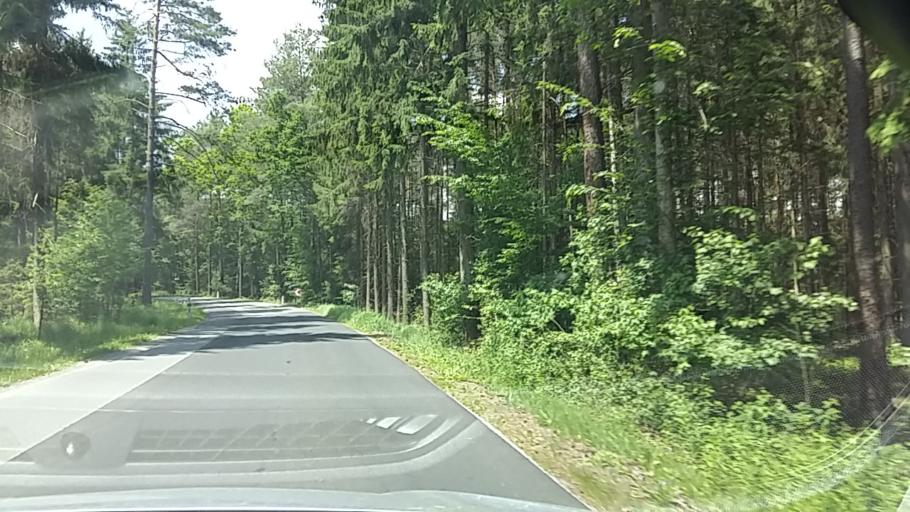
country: AT
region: Styria
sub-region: Politischer Bezirk Hartberg-Fuerstenfeld
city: Bad Blumau
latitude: 47.1237
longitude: 16.0280
